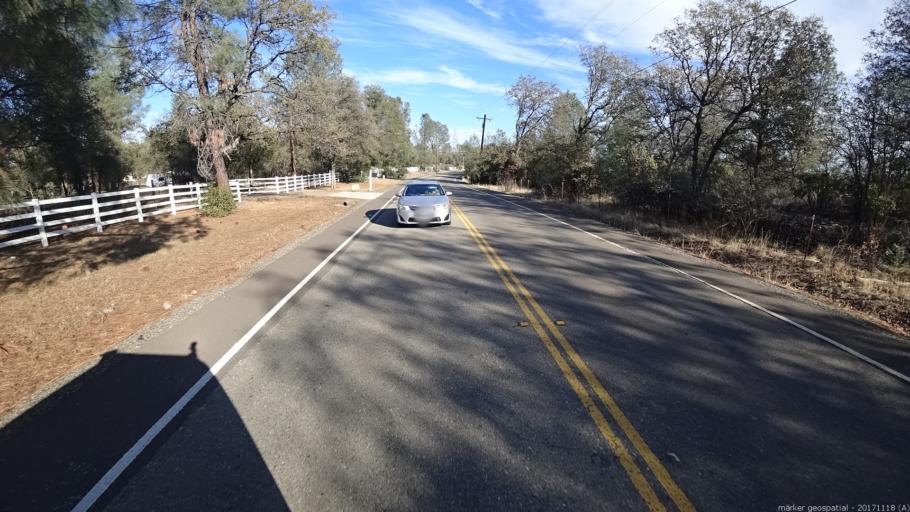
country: US
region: California
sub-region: Shasta County
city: Redding
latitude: 40.4782
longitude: -122.4306
